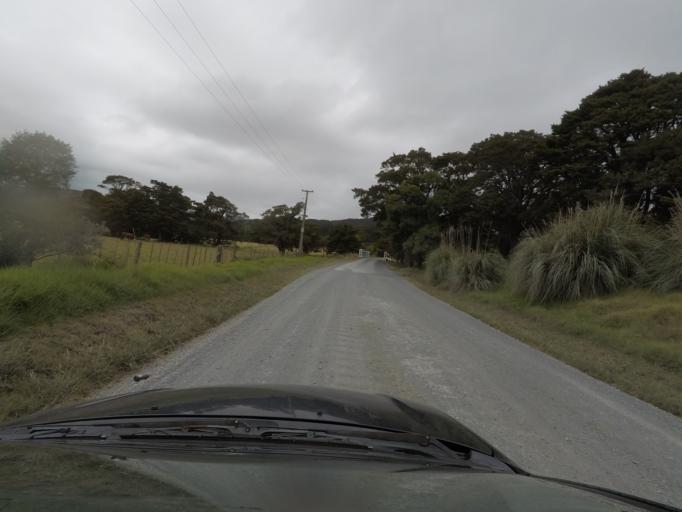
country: NZ
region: Auckland
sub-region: Auckland
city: Warkworth
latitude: -36.2616
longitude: 174.7261
